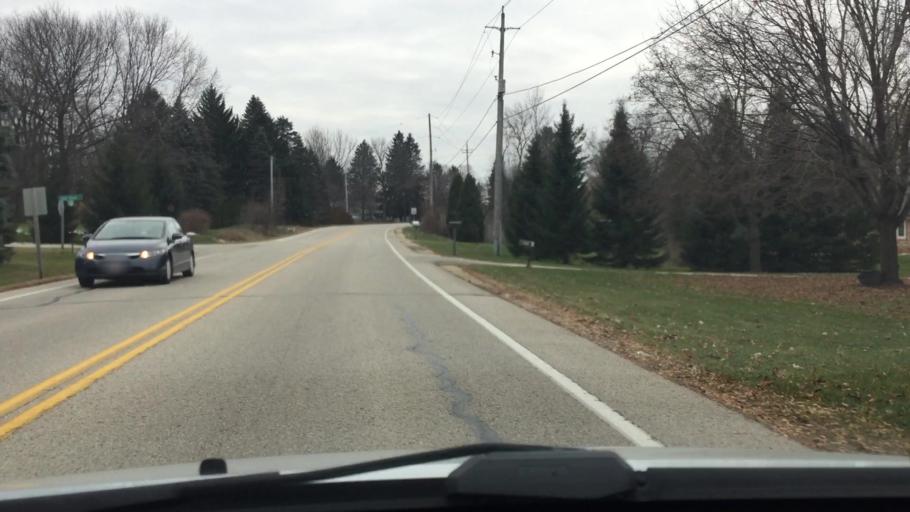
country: US
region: Wisconsin
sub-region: Ozaukee County
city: Grafton
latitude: 43.2979
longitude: -87.9595
